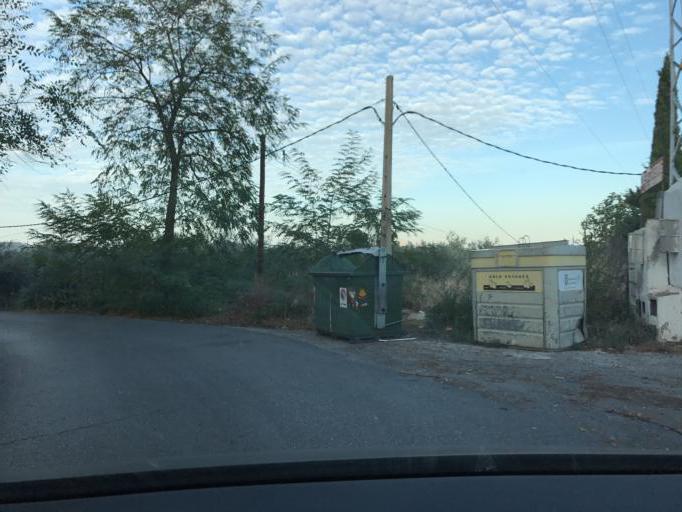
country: ES
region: Andalusia
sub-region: Provincia de Granada
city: Jun
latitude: 37.2223
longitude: -3.5995
